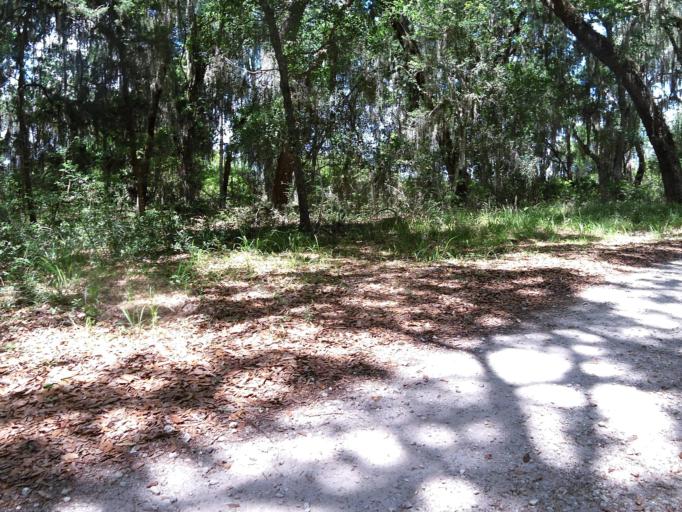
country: US
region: Florida
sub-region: Saint Johns County
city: Villano Beach
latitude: 30.0300
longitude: -81.3372
